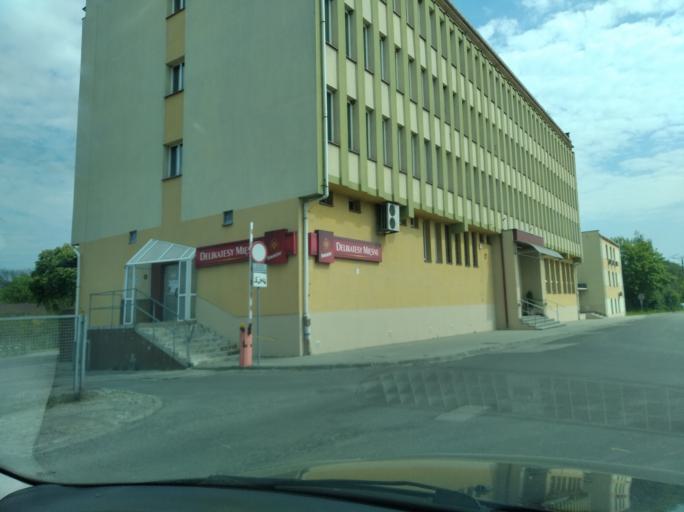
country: PL
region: Subcarpathian Voivodeship
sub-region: Powiat jaroslawski
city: Jaroslaw
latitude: 50.0108
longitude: 22.6701
